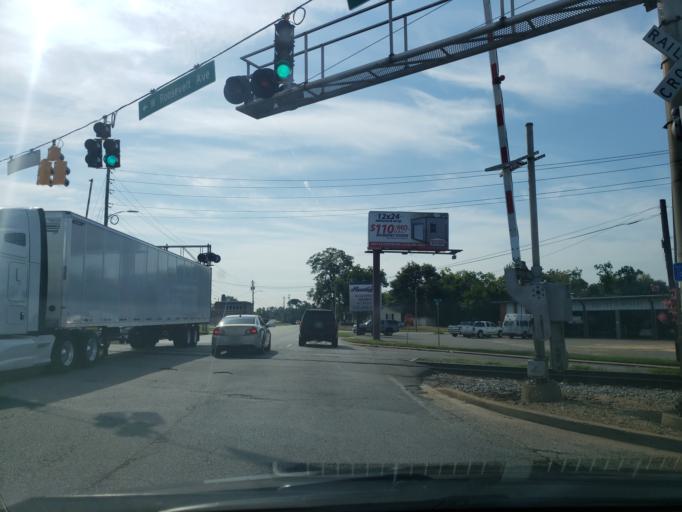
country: US
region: Georgia
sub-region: Dougherty County
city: Albany
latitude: 31.5801
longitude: -84.1740
